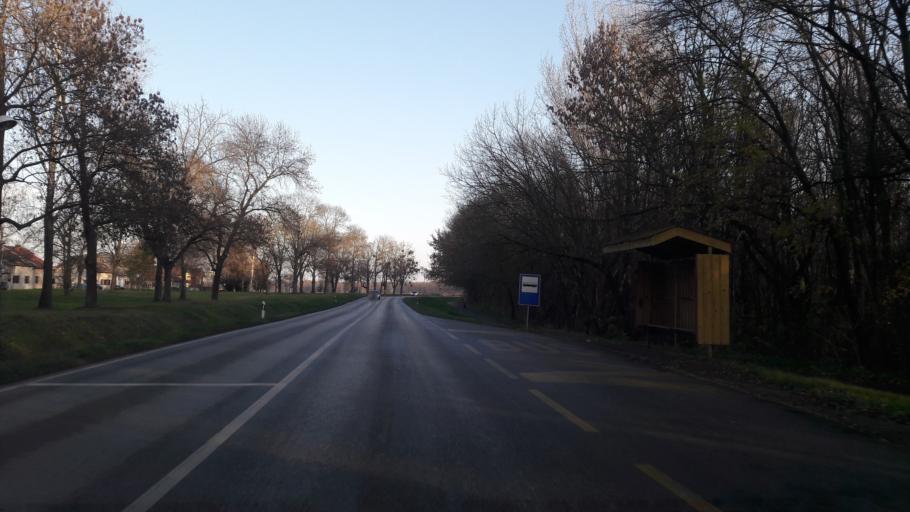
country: HR
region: Osjecko-Baranjska
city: Darda
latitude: 45.6210
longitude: 18.7190
